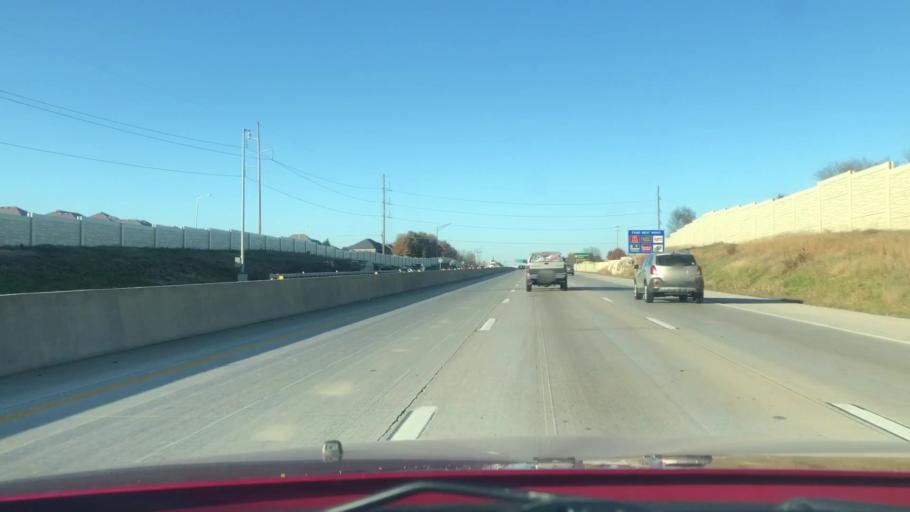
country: US
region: Missouri
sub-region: Greene County
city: Springfield
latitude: 37.1481
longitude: -93.2245
